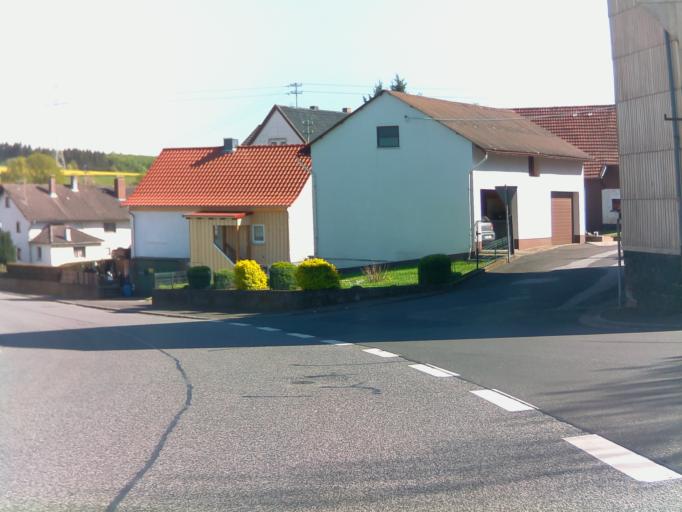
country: DE
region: Hesse
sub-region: Regierungsbezirk Darmstadt
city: Birstein
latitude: 50.3818
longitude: 9.2965
